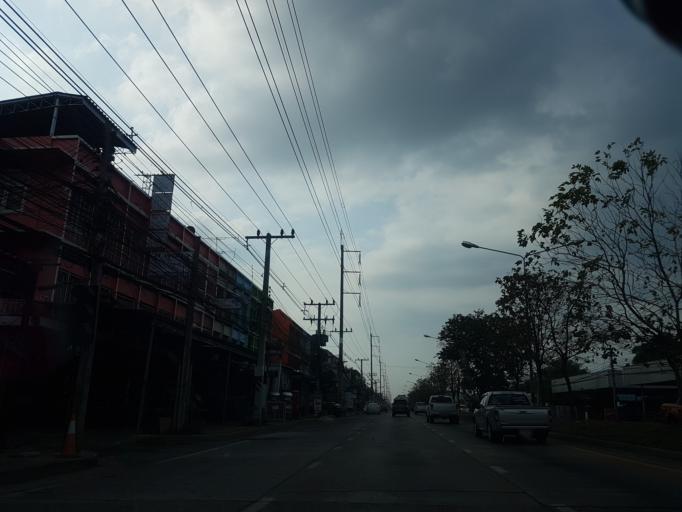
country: TH
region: Sara Buri
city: Phra Phutthabat
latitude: 14.7301
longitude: 100.7873
